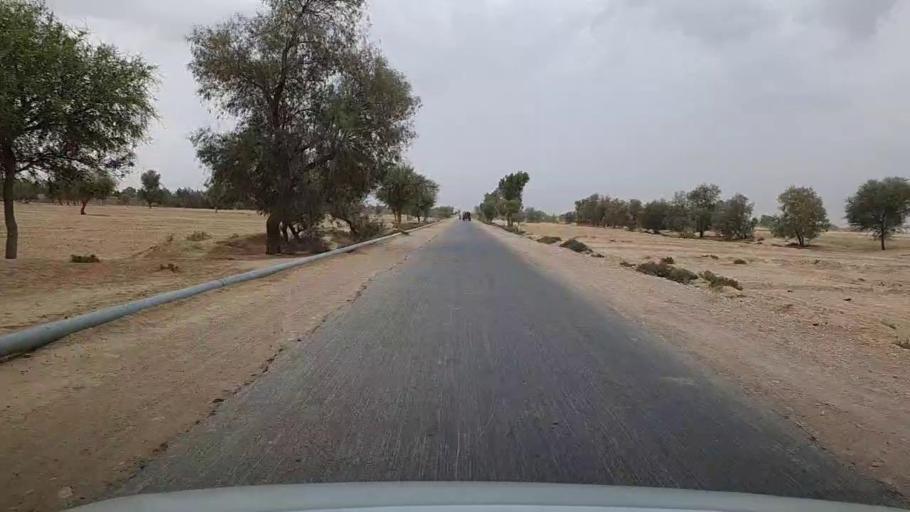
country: PK
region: Sindh
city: Sehwan
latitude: 26.3278
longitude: 67.7253
